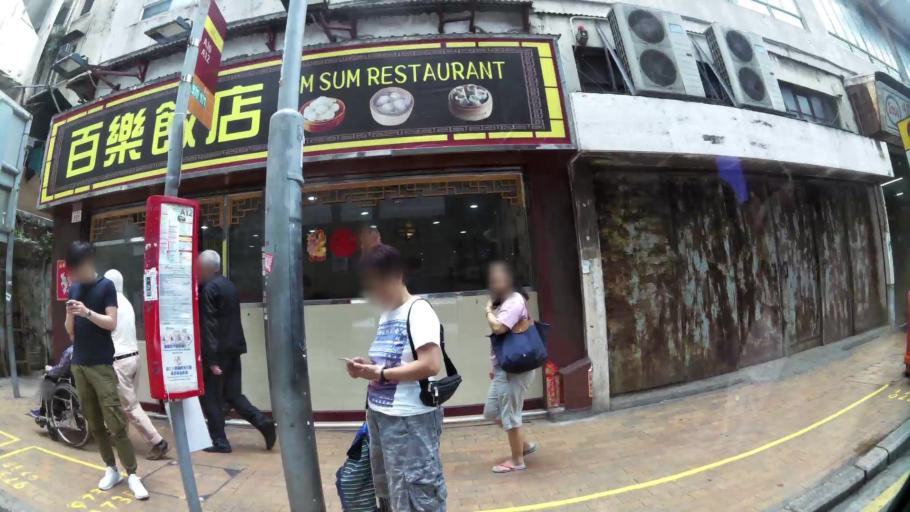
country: HK
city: Hong Kong
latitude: 22.2876
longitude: 114.1386
